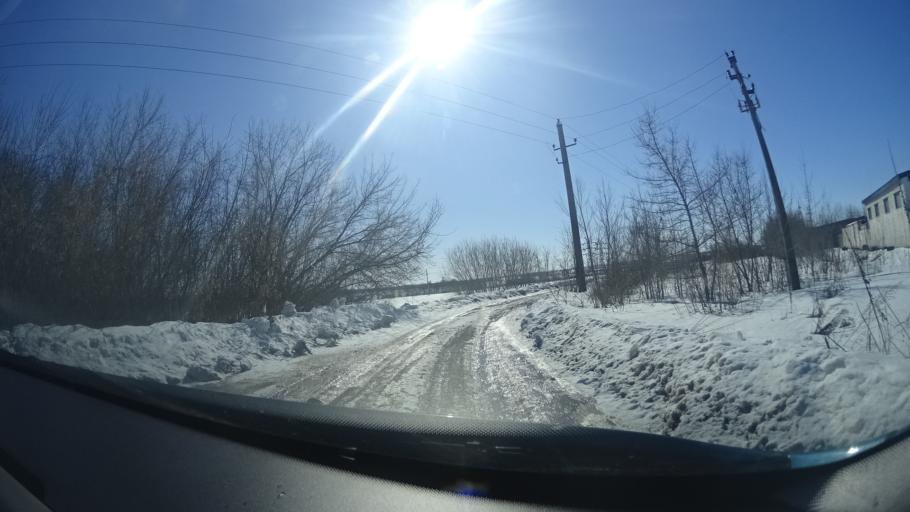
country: RU
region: Bashkortostan
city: Chishmy
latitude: 54.5850
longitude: 55.4022
